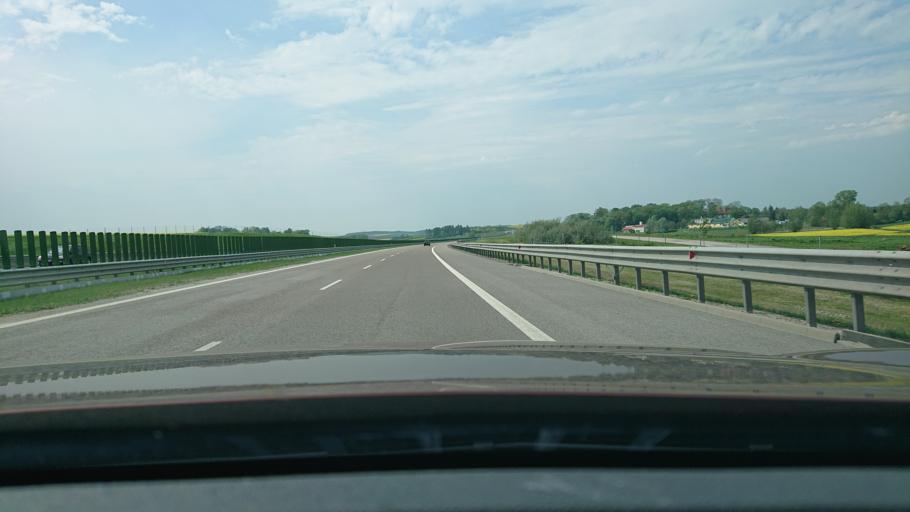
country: PL
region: Subcarpathian Voivodeship
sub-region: Powiat jaroslawski
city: Rokietnica
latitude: 49.9376
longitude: 22.6815
